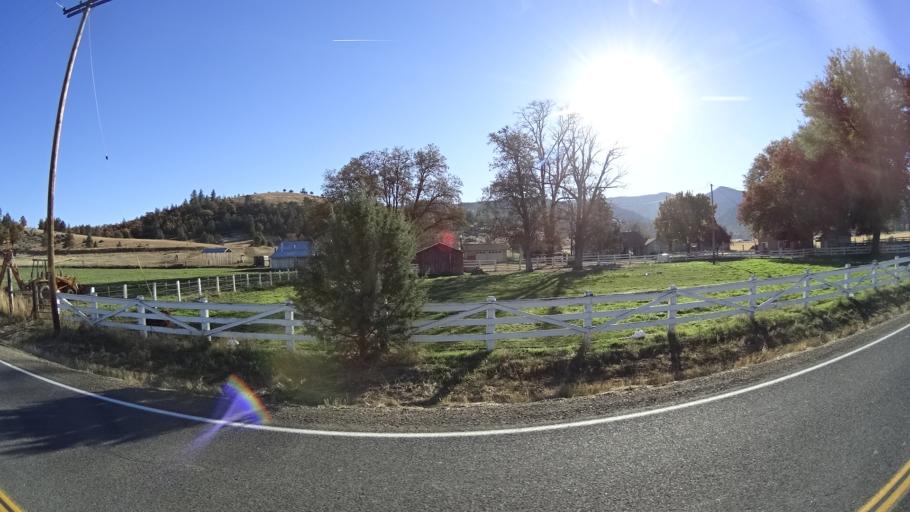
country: US
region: California
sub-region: Siskiyou County
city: Yreka
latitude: 41.5541
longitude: -122.8282
